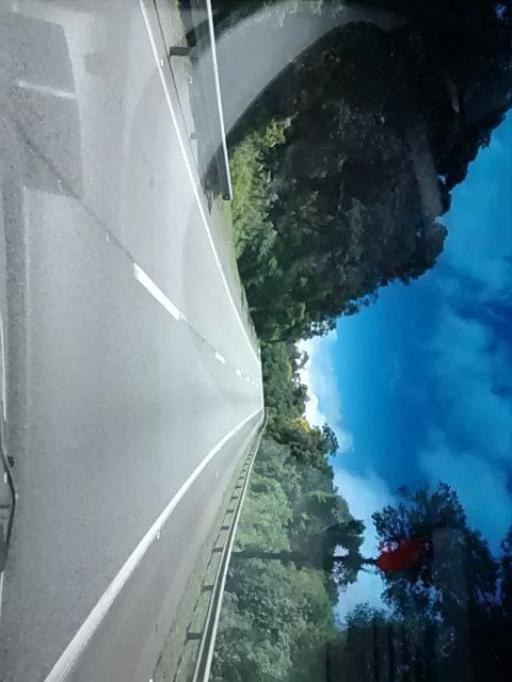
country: BR
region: Parana
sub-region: Antonina
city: Antonina
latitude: -25.1121
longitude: -48.7692
